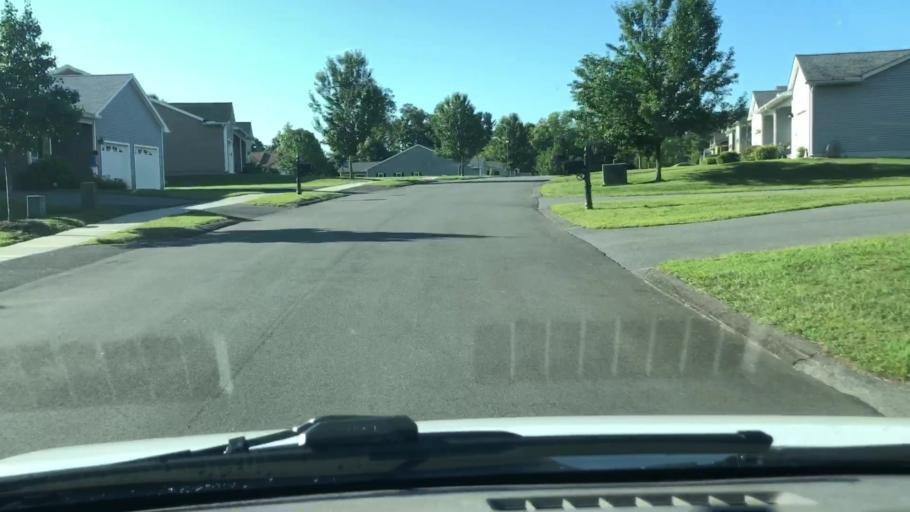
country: US
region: Massachusetts
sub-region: Franklin County
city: Greenfield
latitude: 42.6083
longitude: -72.6034
